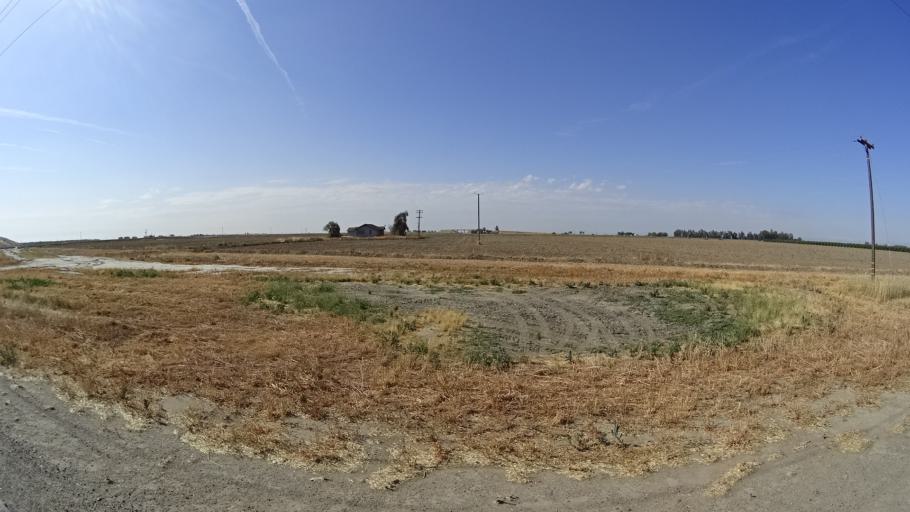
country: US
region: California
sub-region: Kings County
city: Home Garden
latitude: 36.2258
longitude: -119.6115
